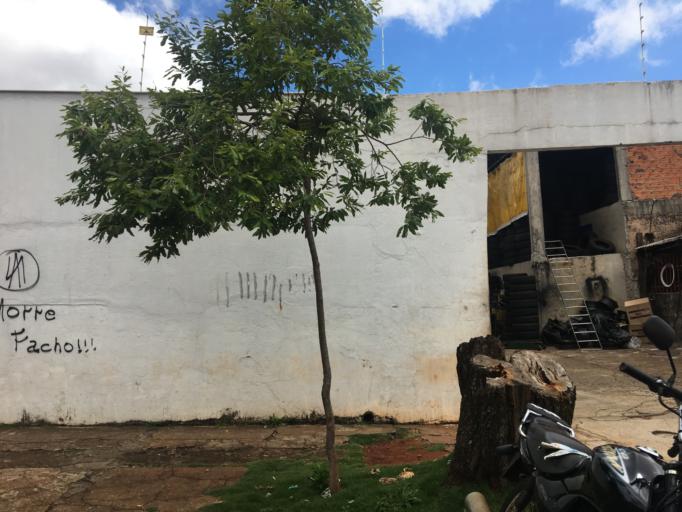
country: BR
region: Parana
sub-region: Londrina
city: Londrina
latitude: -23.3023
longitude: -51.1617
